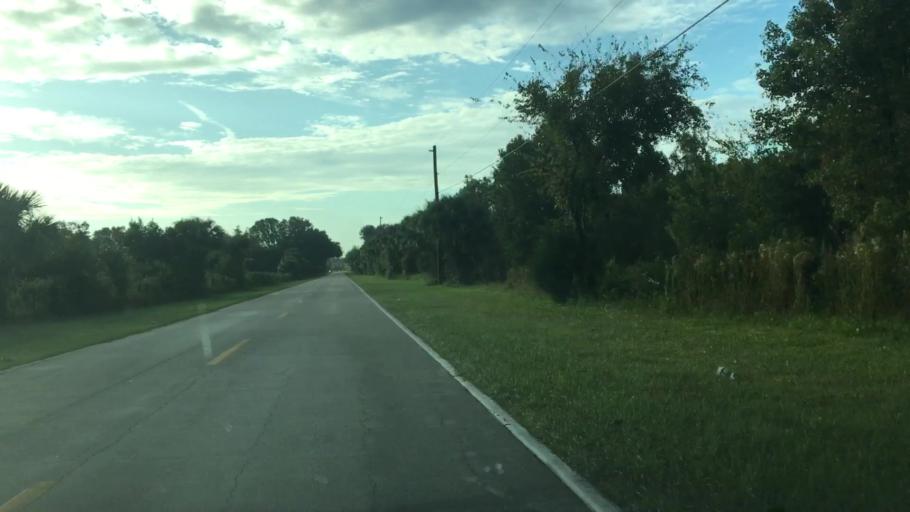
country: US
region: Florida
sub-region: Seminole County
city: Midway
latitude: 28.8271
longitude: -81.1887
